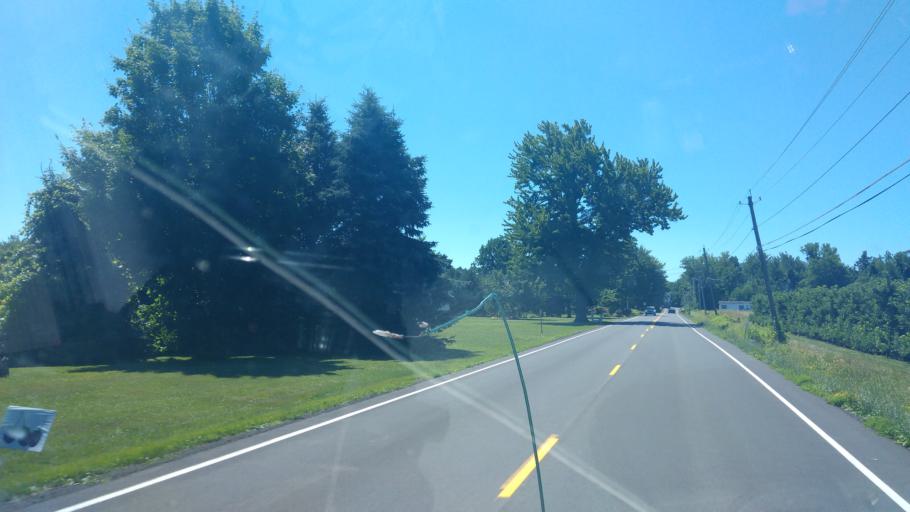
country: US
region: New York
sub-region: Wayne County
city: Sodus
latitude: 43.2159
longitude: -76.9821
